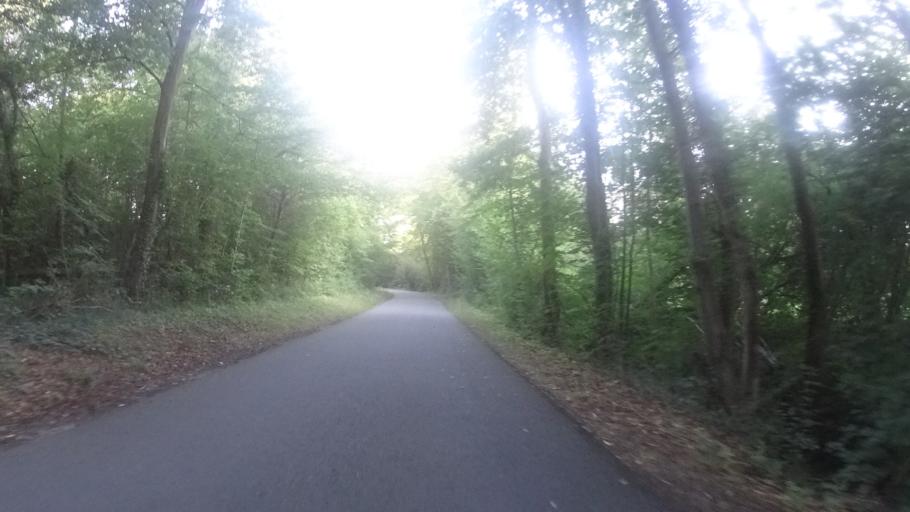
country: FR
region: Picardie
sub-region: Departement de l'Oise
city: Ver-sur-Launette
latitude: 49.1762
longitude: 2.6763
